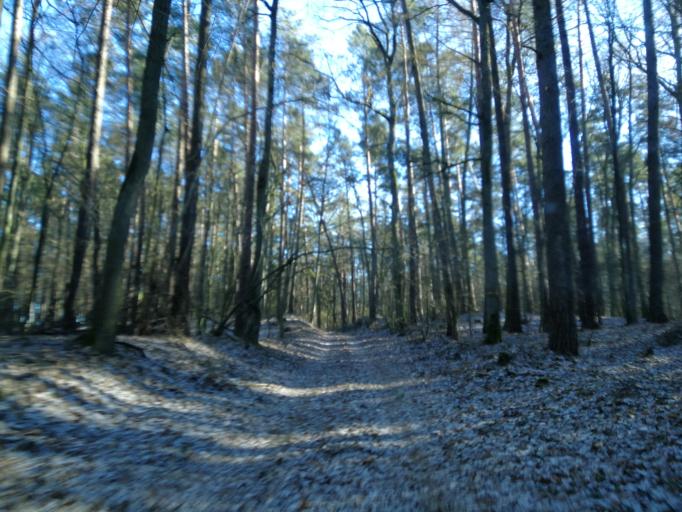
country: PL
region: Kujawsko-Pomorskie
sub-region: Powiat brodnicki
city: Gorzno
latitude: 53.2177
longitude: 19.6734
